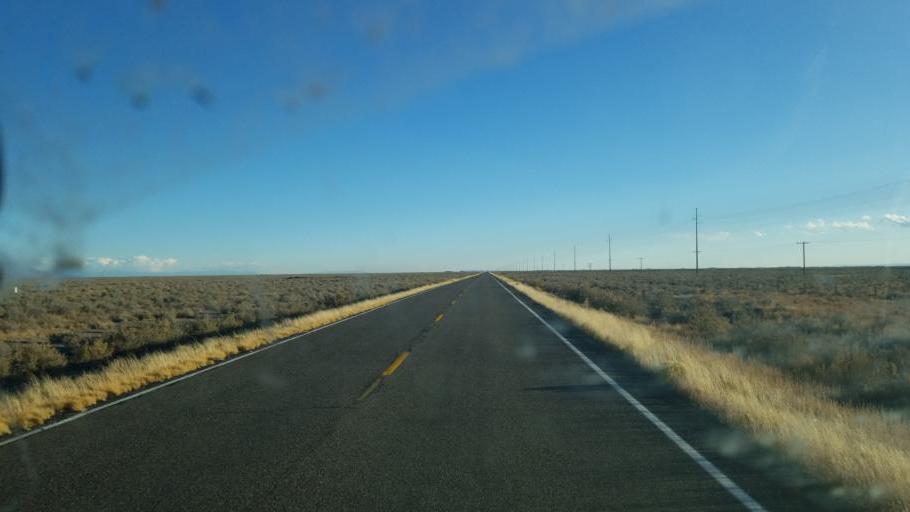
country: US
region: Colorado
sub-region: Saguache County
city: Center
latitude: 37.9107
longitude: -105.8986
